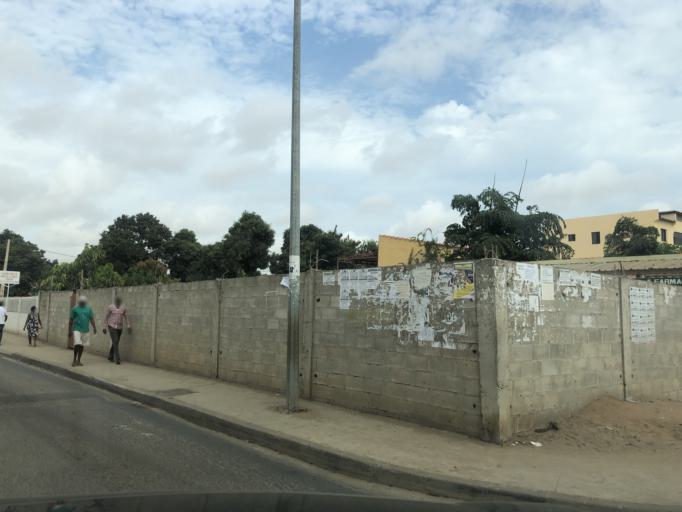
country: AO
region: Luanda
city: Luanda
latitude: -8.9182
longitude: 13.3750
